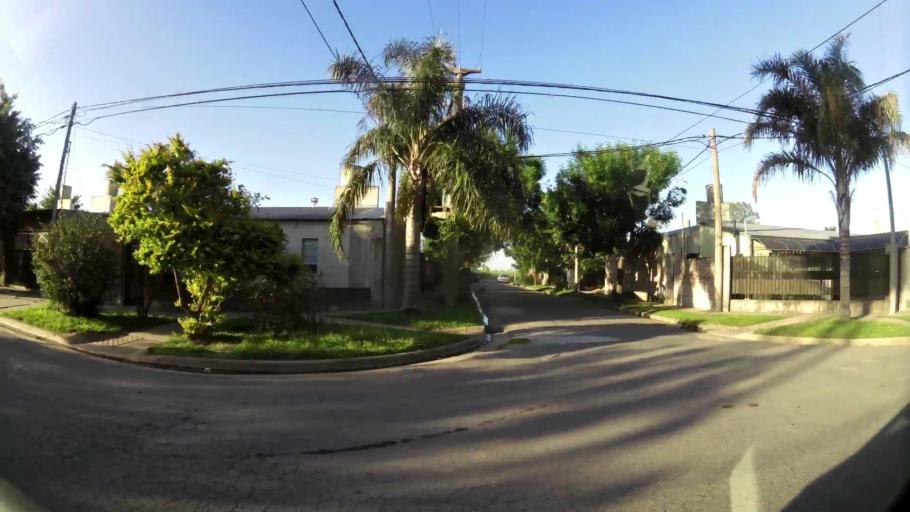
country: AR
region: Santa Fe
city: Santa Fe de la Vera Cruz
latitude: -31.5937
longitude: -60.6793
